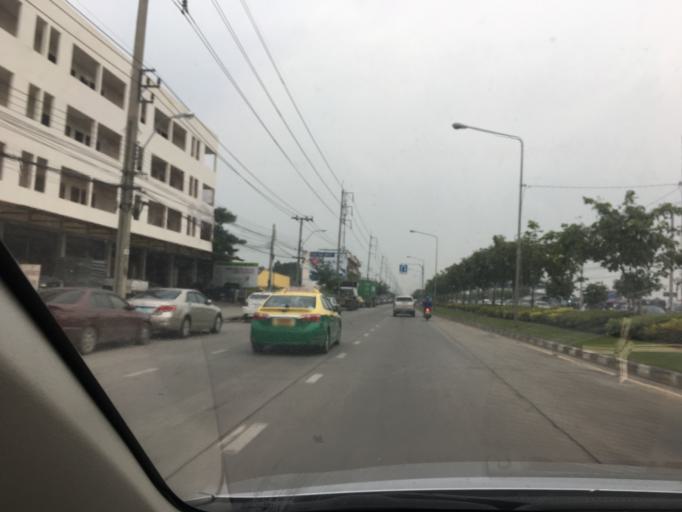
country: TH
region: Bangkok
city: Lat Krabang
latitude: 13.7529
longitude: 100.7752
